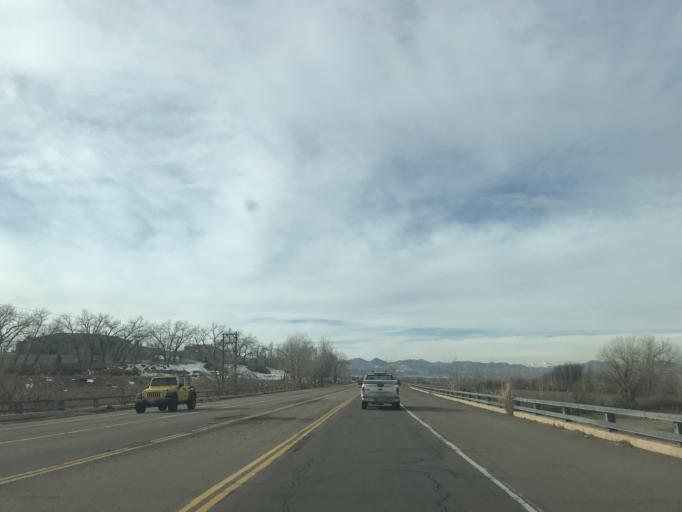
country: US
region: Colorado
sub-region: Arapahoe County
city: Columbine Valley
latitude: 39.5652
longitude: -105.0109
